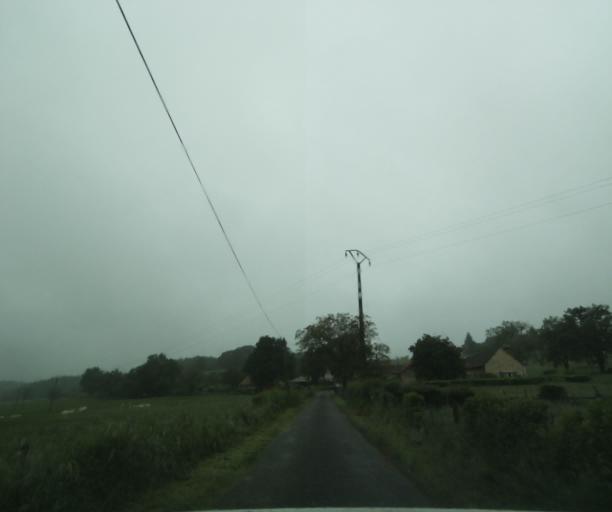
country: FR
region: Bourgogne
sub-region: Departement de Saone-et-Loire
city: Charolles
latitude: 46.4161
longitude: 4.3771
